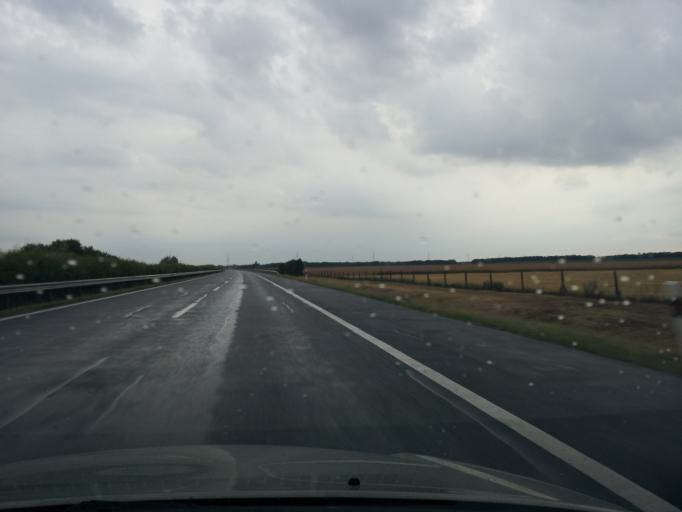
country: HU
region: Borsod-Abauj-Zemplen
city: Emod
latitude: 47.9341
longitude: 20.8597
